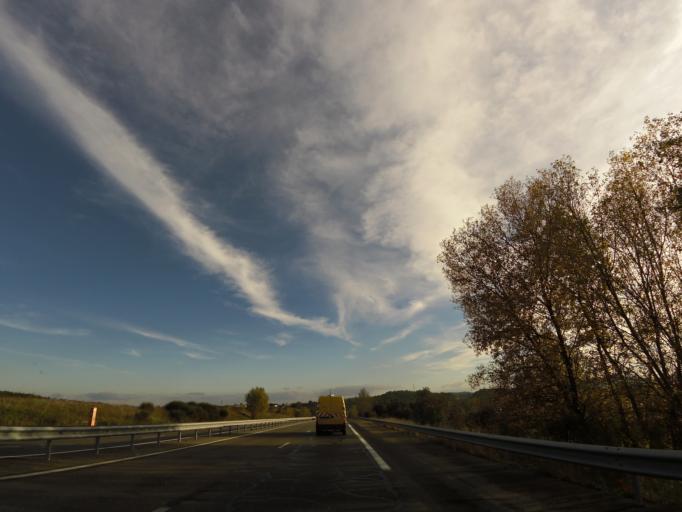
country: FR
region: Languedoc-Roussillon
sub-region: Departement du Gard
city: Vezenobres
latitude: 44.0354
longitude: 4.1451
